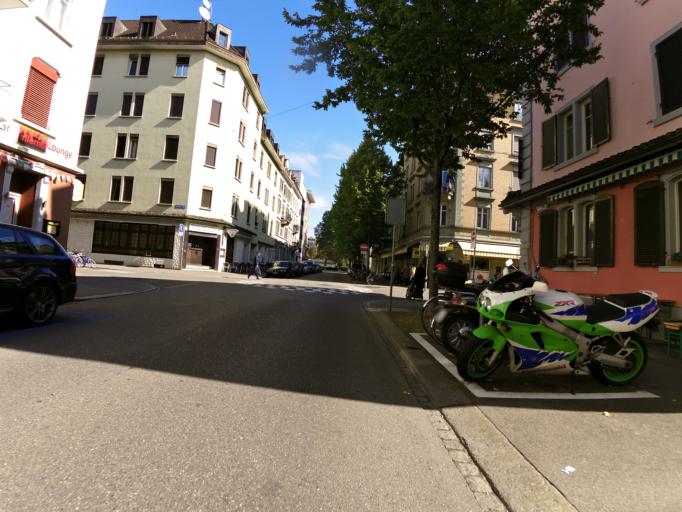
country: CH
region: Zurich
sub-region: Bezirk Zuerich
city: Zuerich (Kreis 5) / Gewerbeschule
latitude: 47.3818
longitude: 8.5334
